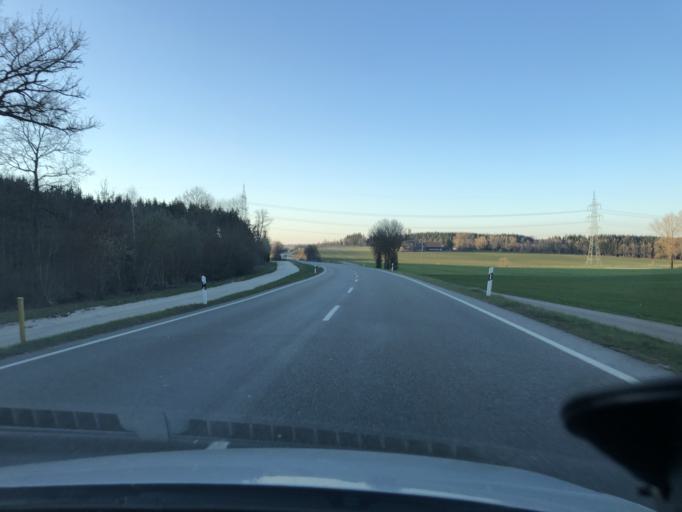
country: DE
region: Baden-Wuerttemberg
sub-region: Freiburg Region
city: Hufingen
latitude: 47.9066
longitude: 8.5076
